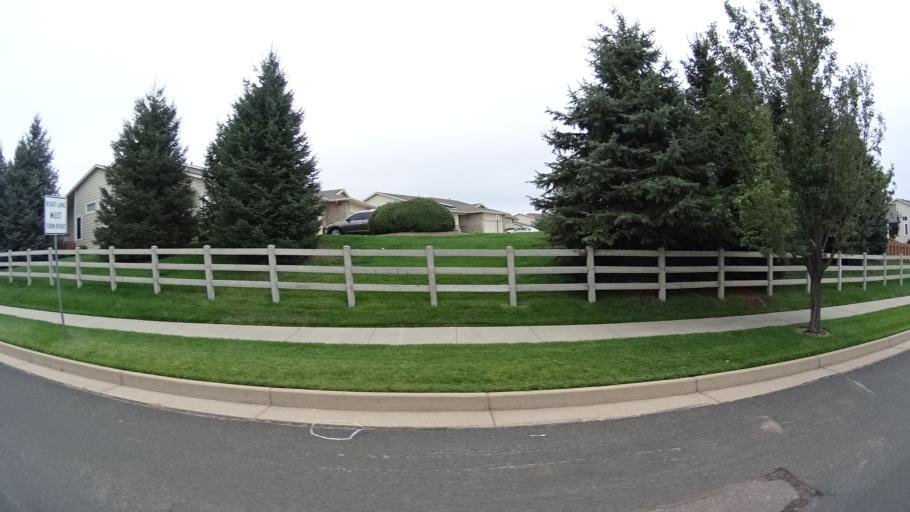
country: US
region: Colorado
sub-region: El Paso County
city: Cimarron Hills
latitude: 38.8899
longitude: -104.7025
